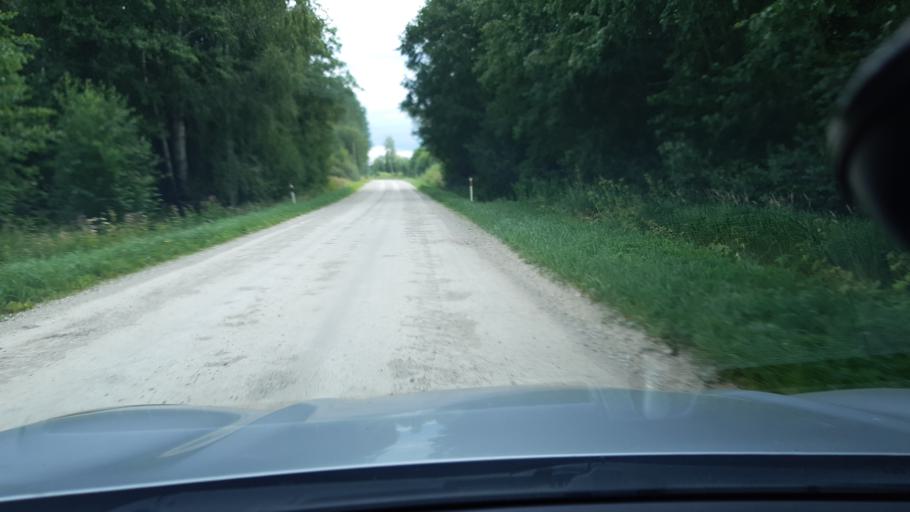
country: EE
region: Raplamaa
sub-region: Jaervakandi vald
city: Jarvakandi
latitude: 58.7956
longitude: 24.9686
